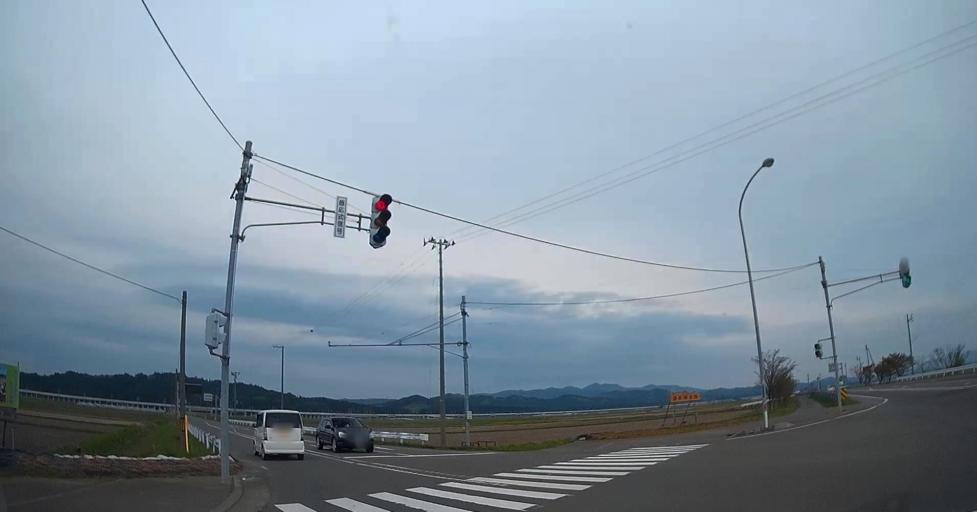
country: JP
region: Aomori
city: Aomori Shi
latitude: 40.9041
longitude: 140.6647
